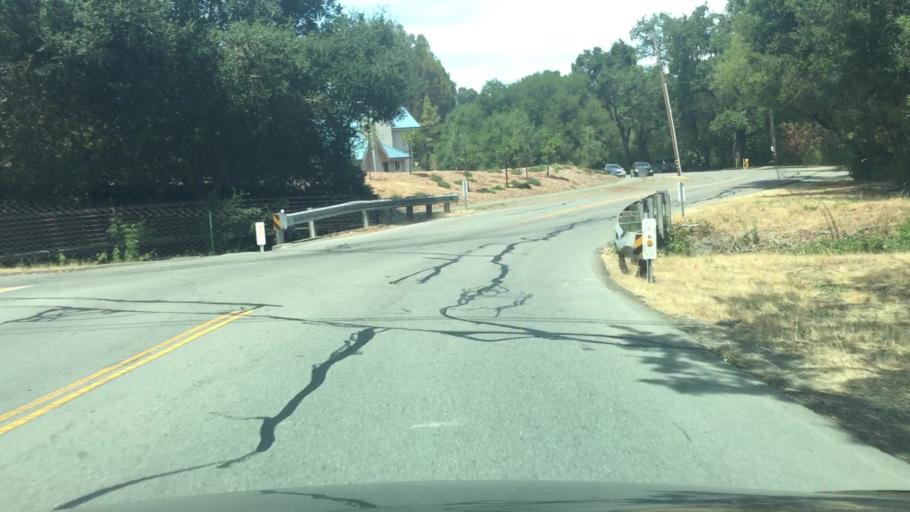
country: US
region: California
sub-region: Santa Clara County
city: Los Altos Hills
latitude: 37.3815
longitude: -122.1656
